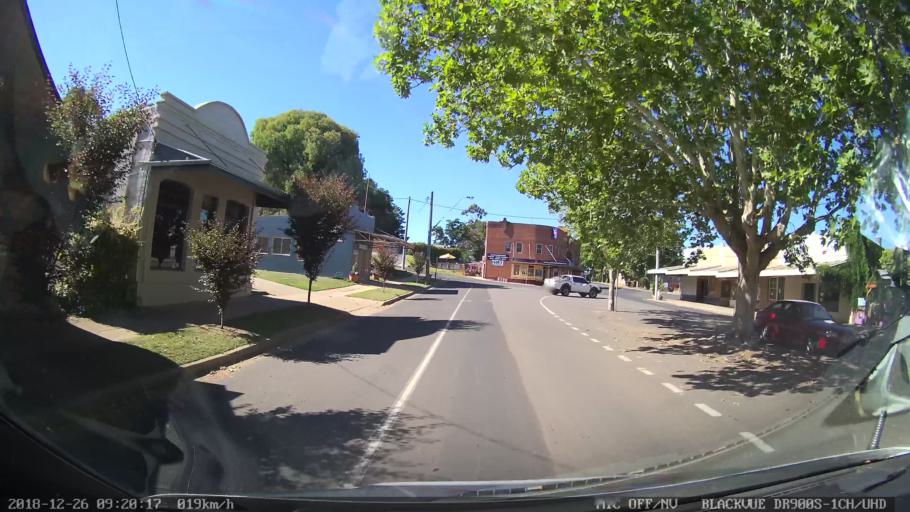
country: AU
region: New South Wales
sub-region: Mid-Western Regional
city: Kandos
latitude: -32.7969
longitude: 149.9712
